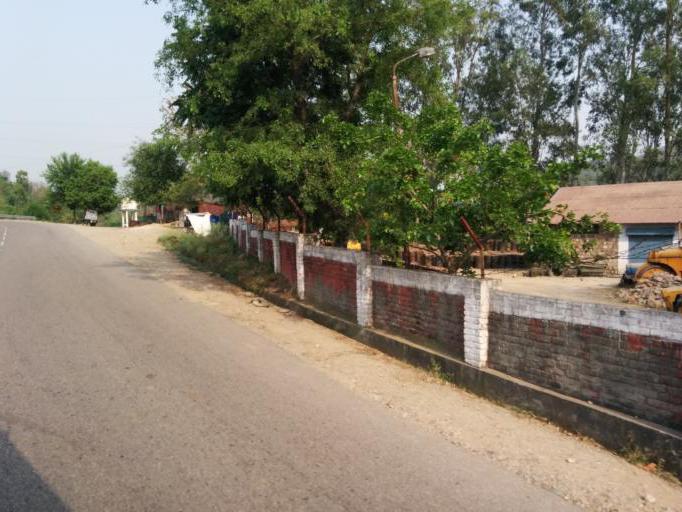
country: IN
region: Punjab
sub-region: Gurdaspur
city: Dharkalan
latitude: 32.2878
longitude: 75.8715
